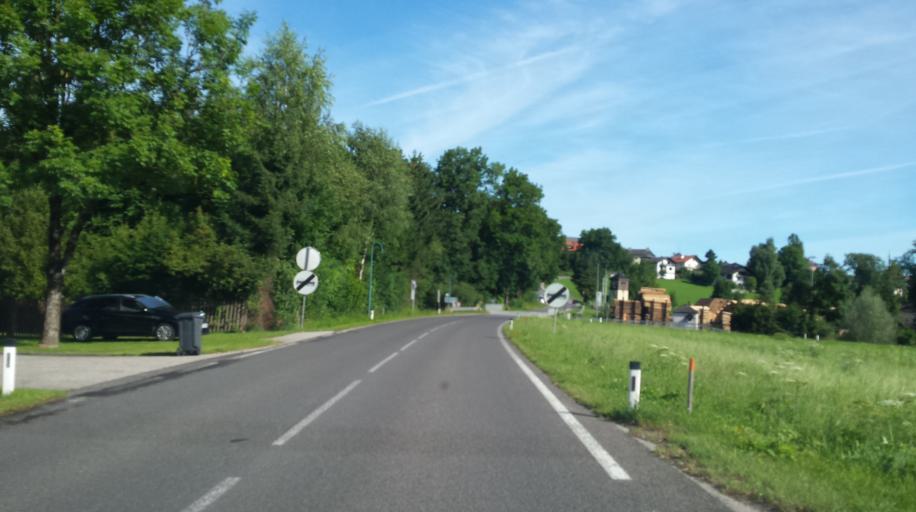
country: AT
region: Upper Austria
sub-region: Politischer Bezirk Vocklabruck
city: Frankenmarkt
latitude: 47.9803
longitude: 13.4175
